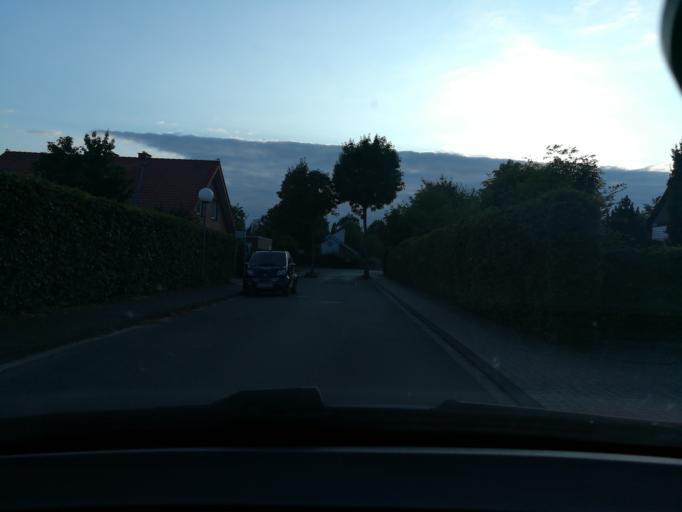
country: DE
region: North Rhine-Westphalia
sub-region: Regierungsbezirk Munster
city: Lienen
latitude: 52.1438
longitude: 7.9756
